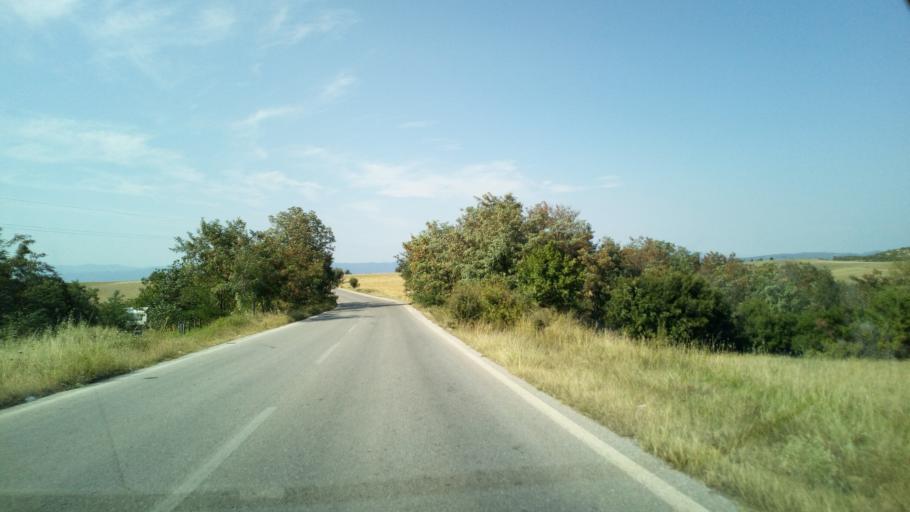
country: GR
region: Central Macedonia
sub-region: Nomos Chalkidikis
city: Arnaia
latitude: 40.5071
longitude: 23.4746
